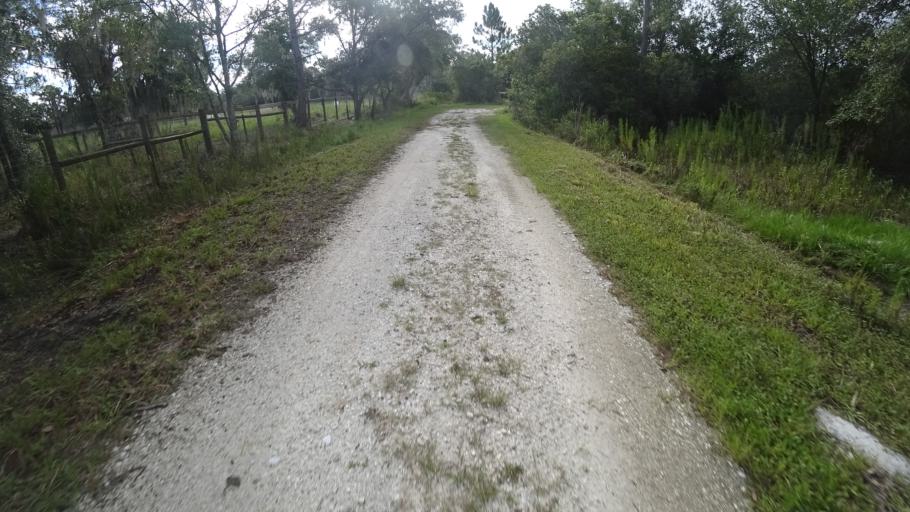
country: US
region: Florida
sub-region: Sarasota County
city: Fruitville
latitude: 27.4087
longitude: -82.2774
